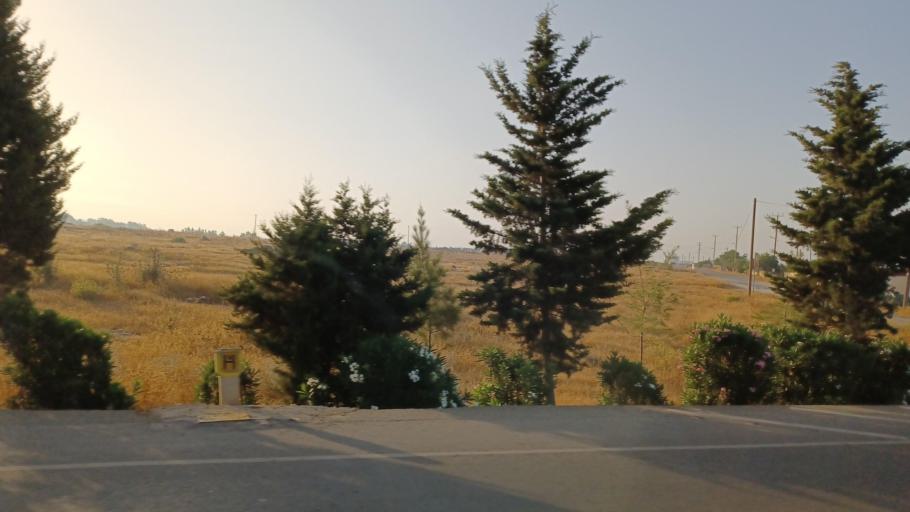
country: CY
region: Ammochostos
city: Frenaros
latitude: 35.0115
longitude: 33.9390
